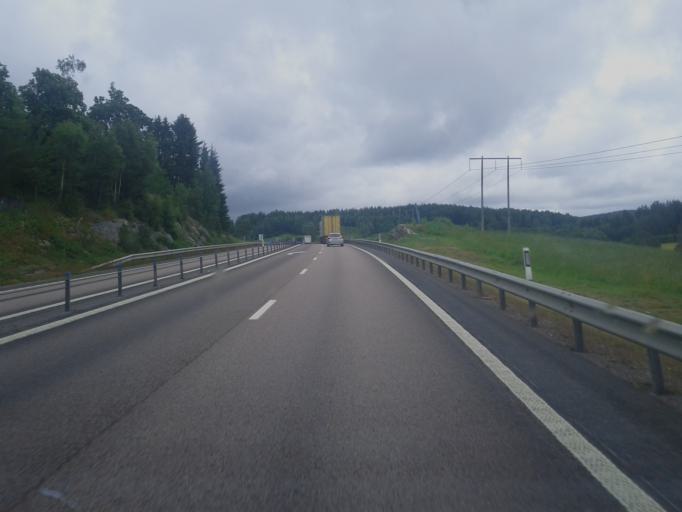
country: SE
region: Vaesternorrland
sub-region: Haernoesands Kommun
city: Haernoesand
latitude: 62.5853
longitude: 17.7798
